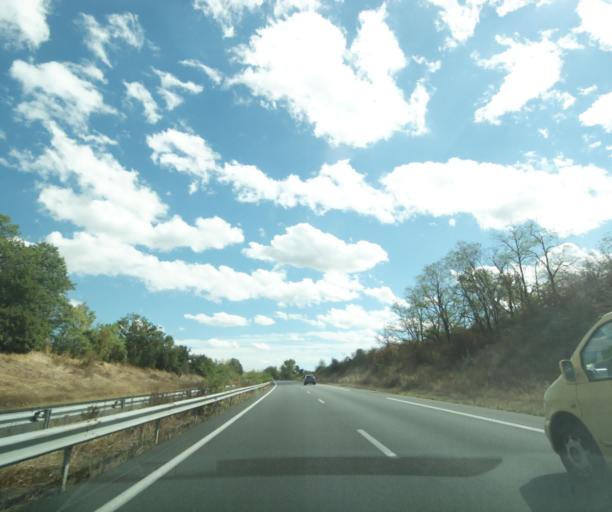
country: FR
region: Aquitaine
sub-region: Departement du Lot-et-Garonne
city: Fourques-sur-Garonne
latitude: 44.4532
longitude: 0.0880
